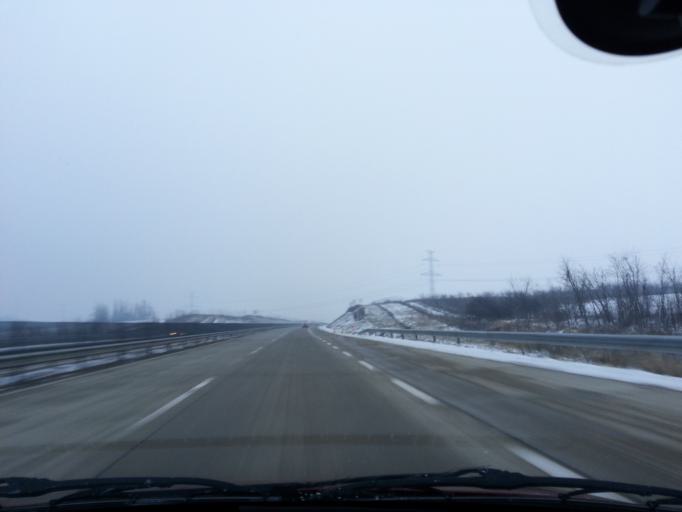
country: HU
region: Pest
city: Kerepes
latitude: 47.5534
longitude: 19.3154
